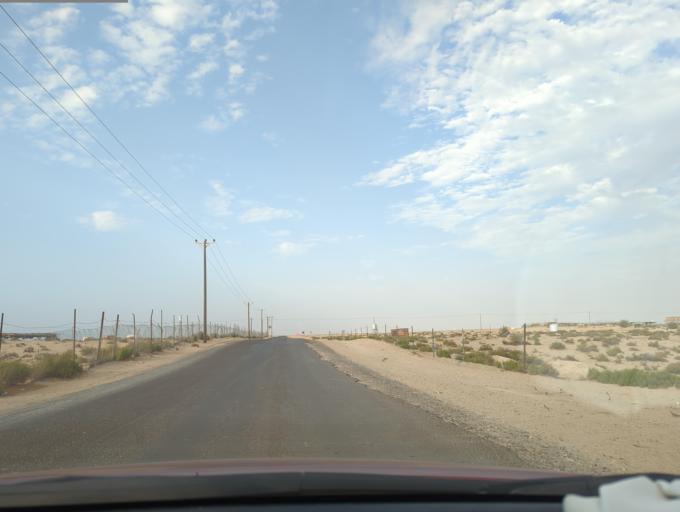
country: AE
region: Dubai
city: Dubai
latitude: 24.7179
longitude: 54.8698
